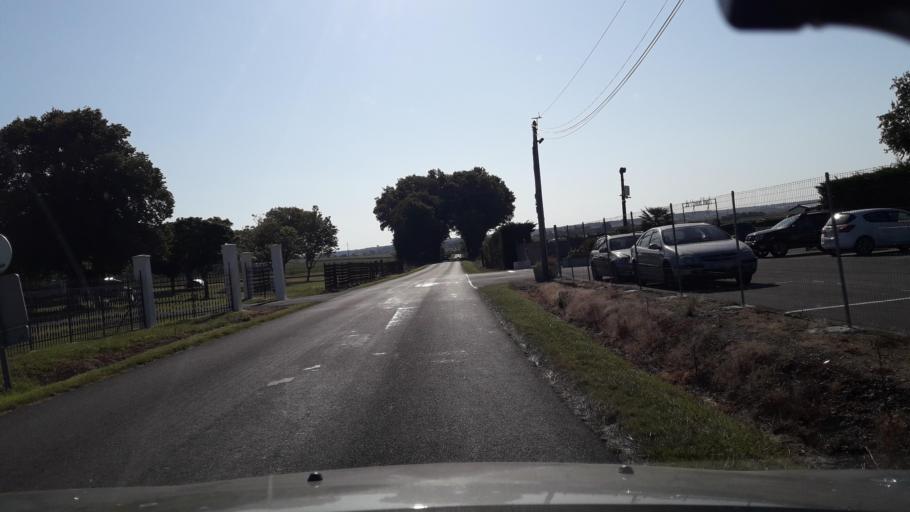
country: FR
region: Poitou-Charentes
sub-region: Departement de la Charente-Maritime
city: Les Mathes
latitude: 45.7127
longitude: -1.1284
